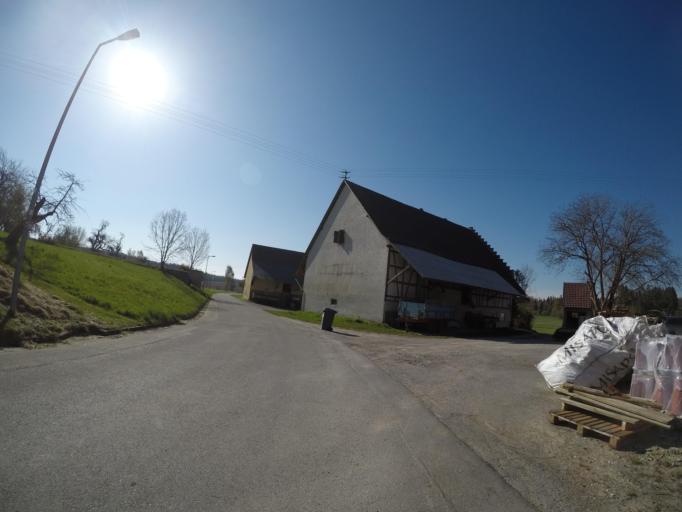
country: DE
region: Baden-Wuerttemberg
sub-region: Tuebingen Region
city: Altshausen
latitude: 47.9223
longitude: 9.5203
